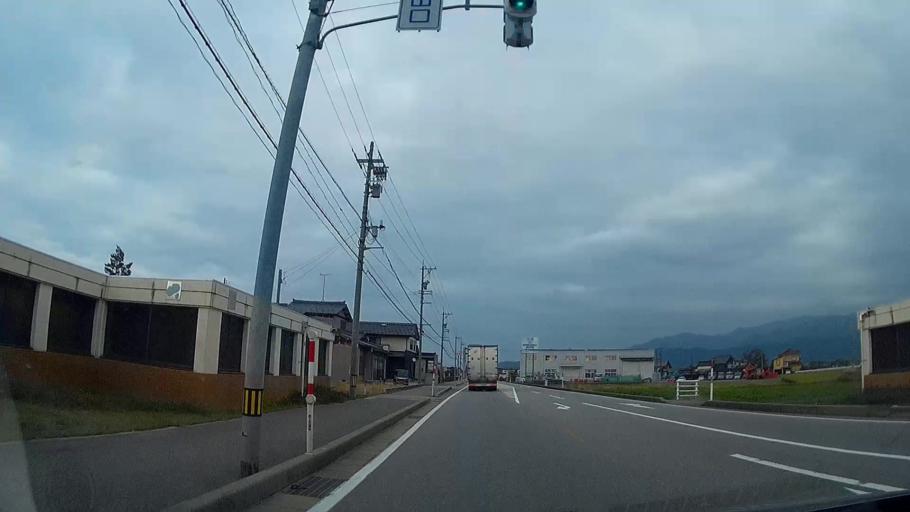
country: JP
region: Toyama
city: Nyuzen
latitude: 36.9407
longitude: 137.5167
